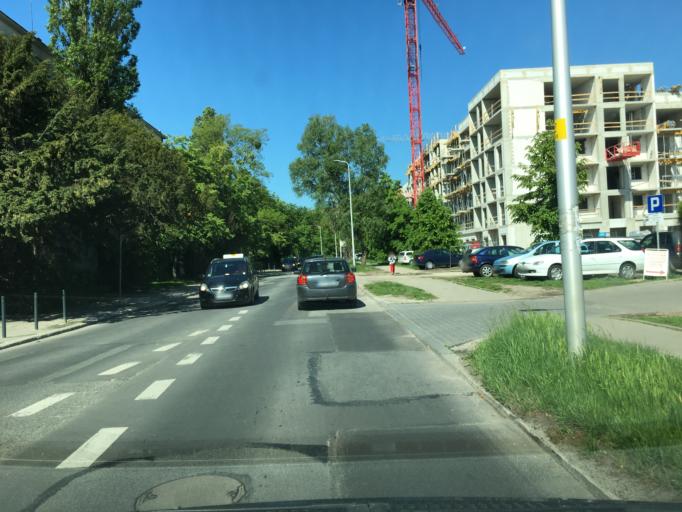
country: PL
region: Lower Silesian Voivodeship
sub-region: Powiat wroclawski
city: Wroclaw
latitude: 51.0948
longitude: 16.9908
